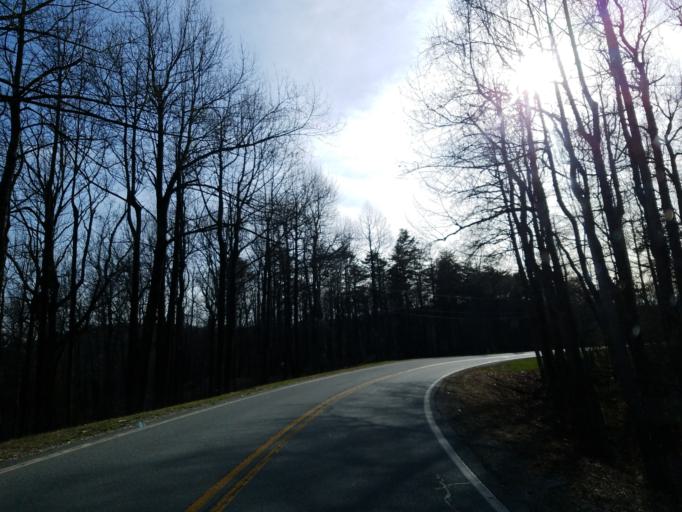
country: US
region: Georgia
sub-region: Pickens County
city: Jasper
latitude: 34.5420
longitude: -84.3304
